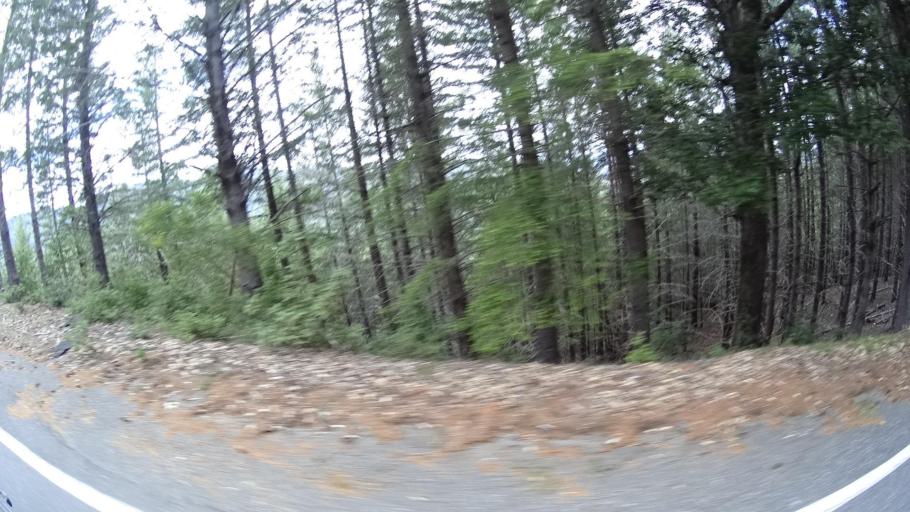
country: US
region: California
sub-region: Humboldt County
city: Redway
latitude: 40.0507
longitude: -124.0078
